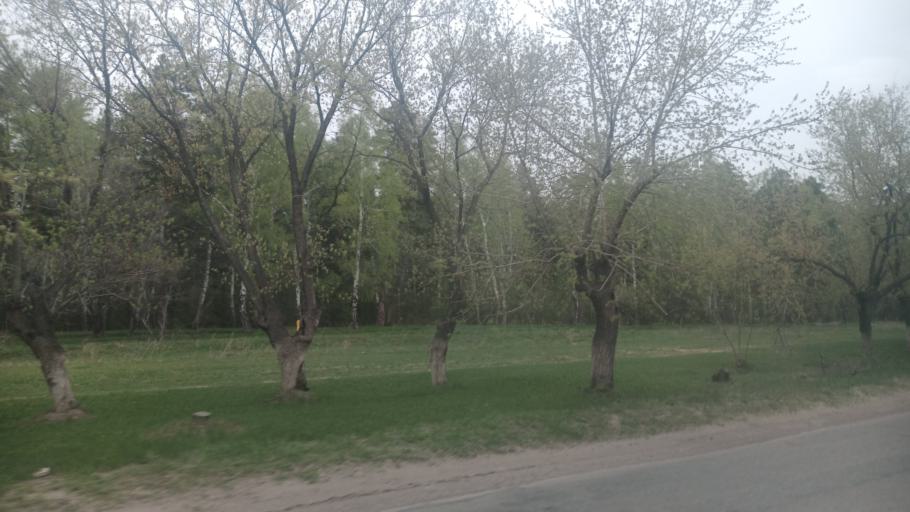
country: RU
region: Altai Krai
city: Yuzhnyy
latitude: 53.2560
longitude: 83.6861
